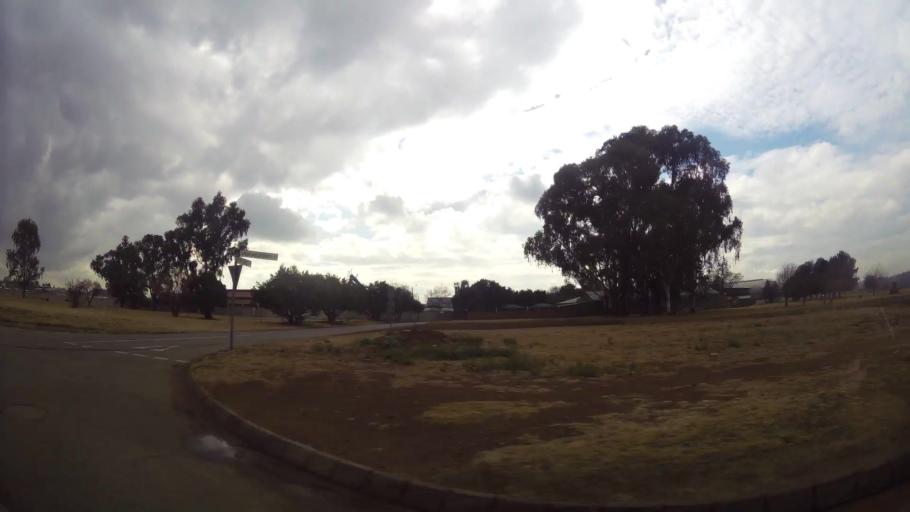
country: ZA
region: Gauteng
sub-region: Sedibeng District Municipality
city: Meyerton
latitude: -26.5800
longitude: 28.0121
